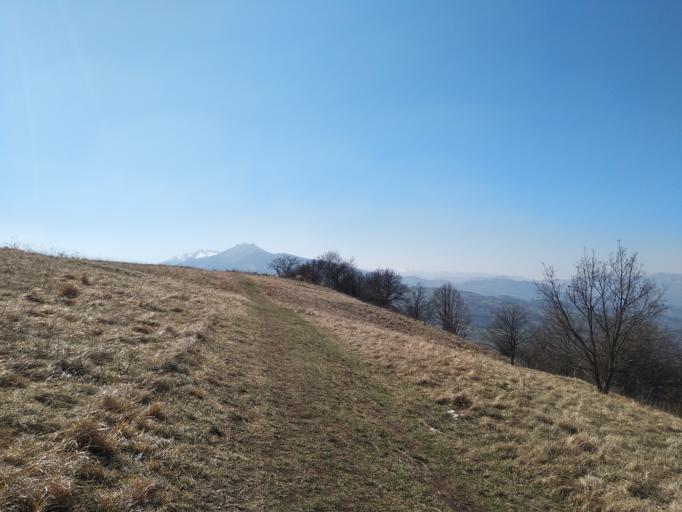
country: IT
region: Emilia-Romagna
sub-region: Provincia di Reggio Emilia
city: Castelnovo ne'Monti
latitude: 44.4202
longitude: 10.4103
